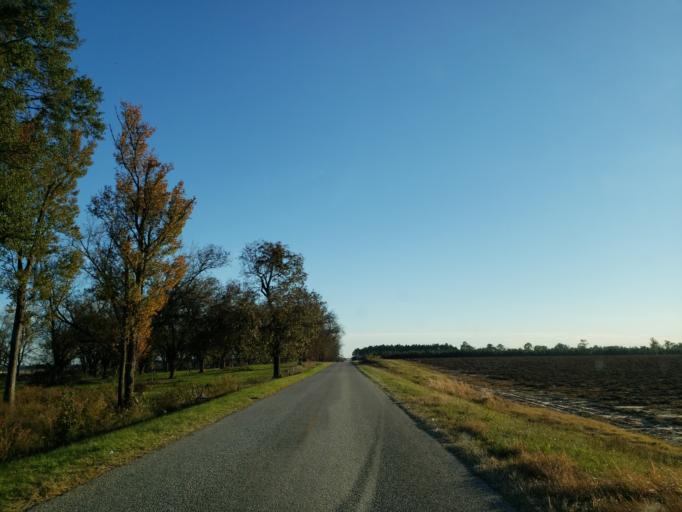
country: US
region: Georgia
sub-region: Dooly County
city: Vienna
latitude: 32.1569
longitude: -83.7605
